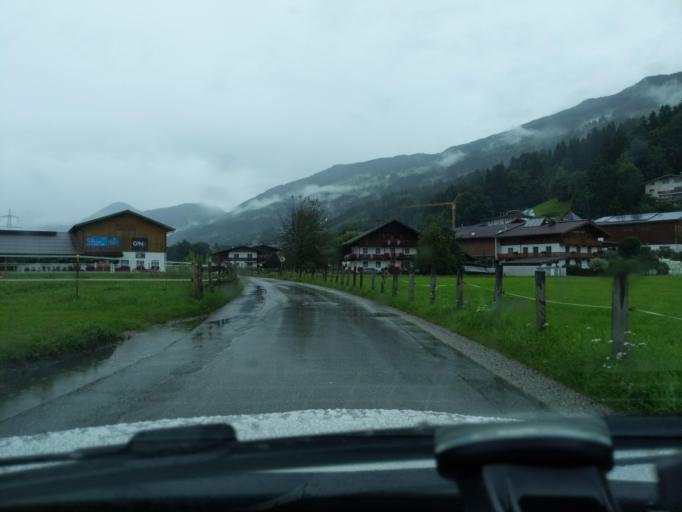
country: AT
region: Tyrol
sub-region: Politischer Bezirk Schwaz
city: Hart im Zillertal
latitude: 47.3361
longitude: 11.8678
